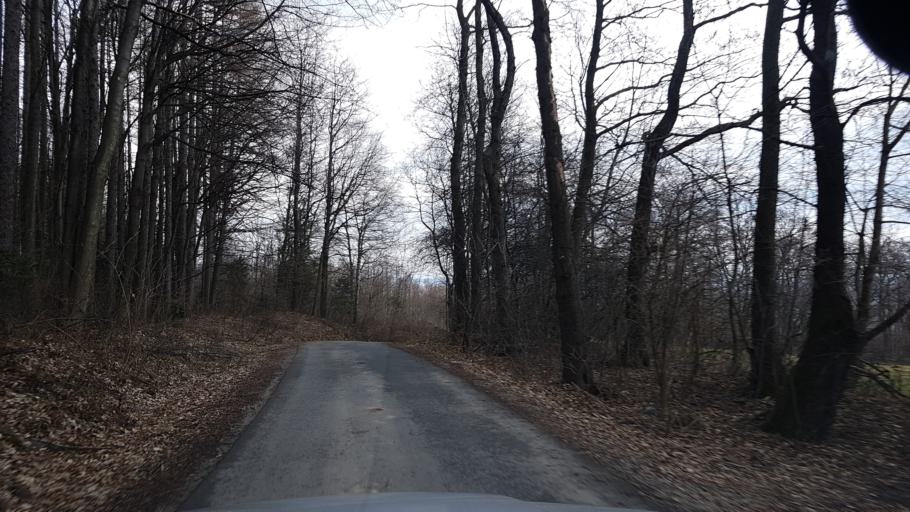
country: PL
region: Lesser Poland Voivodeship
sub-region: Powiat nowosadecki
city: Stary Sacz
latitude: 49.5370
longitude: 20.6362
